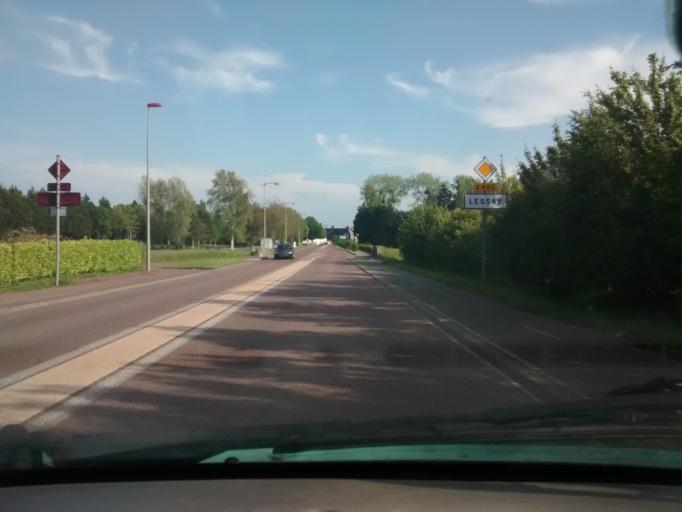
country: FR
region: Lower Normandy
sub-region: Departement de la Manche
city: Lessay
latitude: 49.2235
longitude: -1.5332
